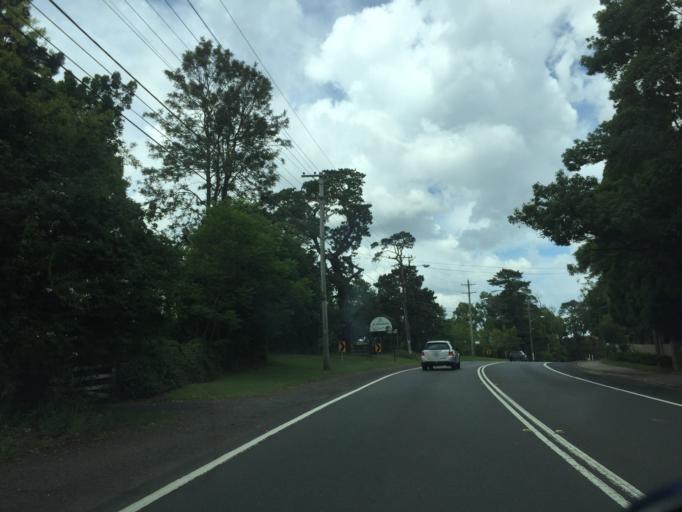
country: AU
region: New South Wales
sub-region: The Hills Shire
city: Glenhaven
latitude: -33.7044
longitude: 151.0143
